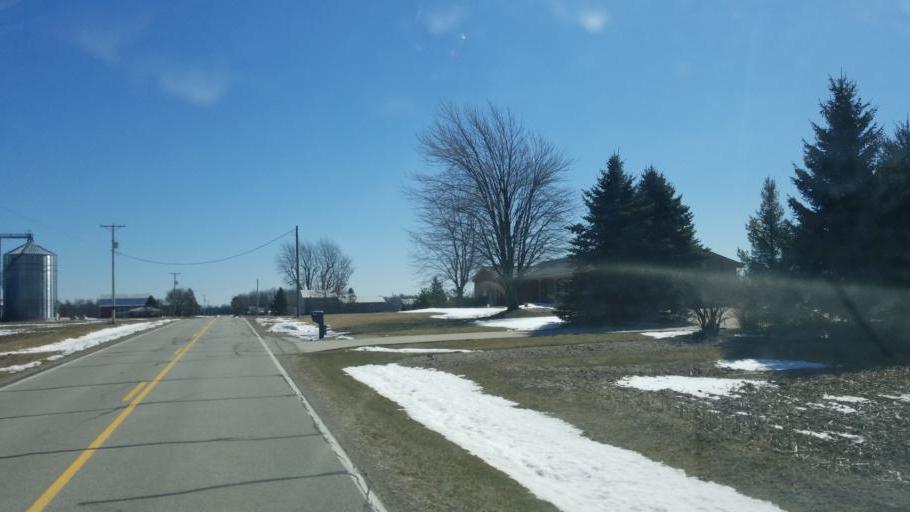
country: US
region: Ohio
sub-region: Crawford County
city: Bucyrus
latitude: 40.8048
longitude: -83.0461
